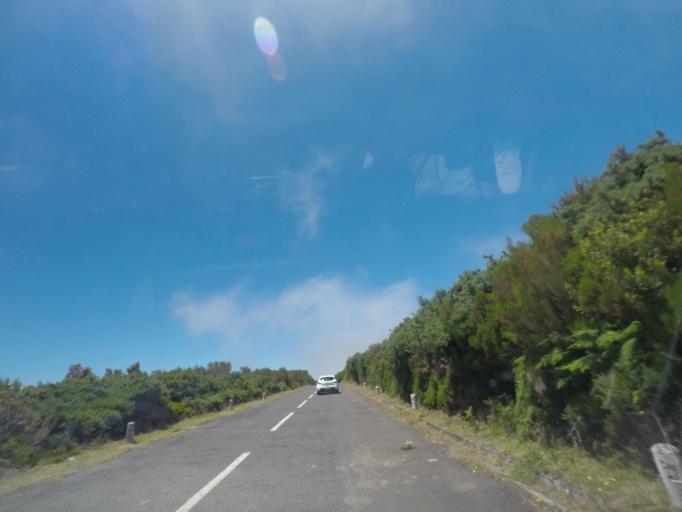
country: PT
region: Madeira
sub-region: Porto Moniz
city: Porto Moniz
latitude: 32.8059
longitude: -17.1920
